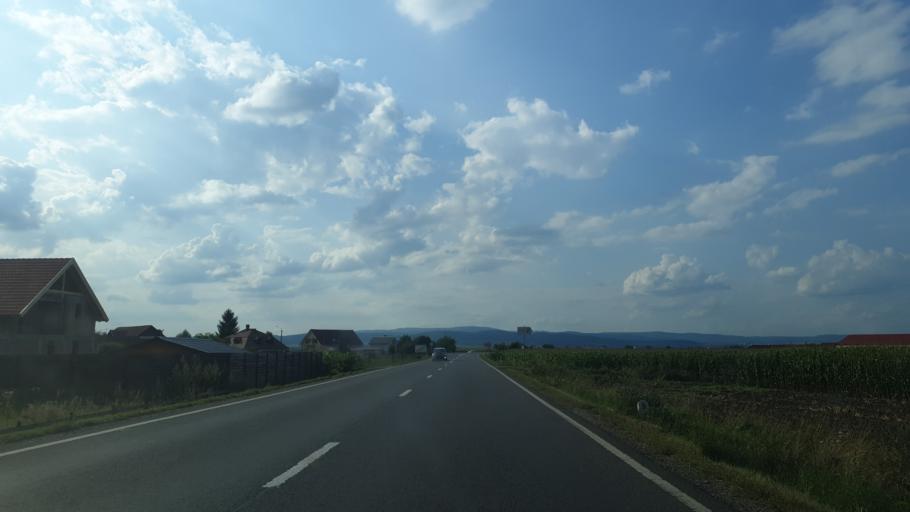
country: RO
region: Covasna
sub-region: Comuna Chichis
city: Chichis
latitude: 45.7789
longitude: 25.8080
